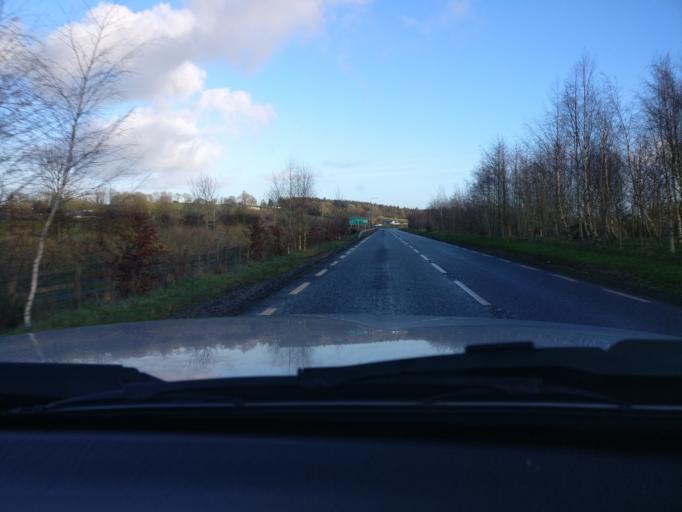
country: IE
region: Leinster
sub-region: An Mhi
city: Kells
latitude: 53.7407
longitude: -6.8728
